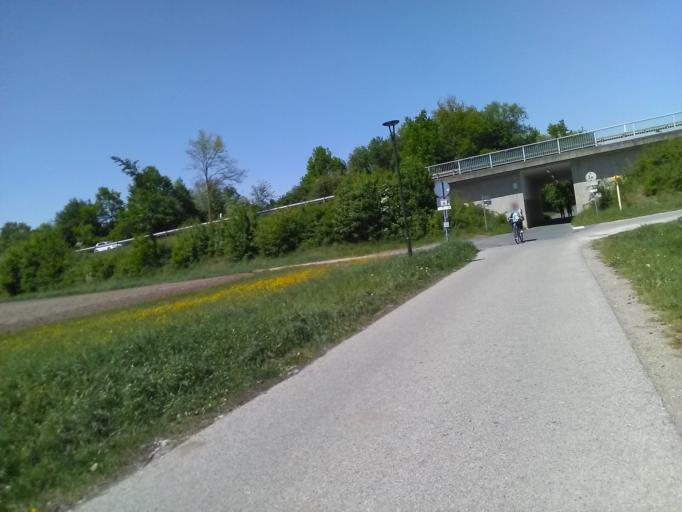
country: DE
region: Bavaria
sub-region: Regierungsbezirk Mittelfranken
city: Gunzenhausen
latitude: 49.1226
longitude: 10.7481
